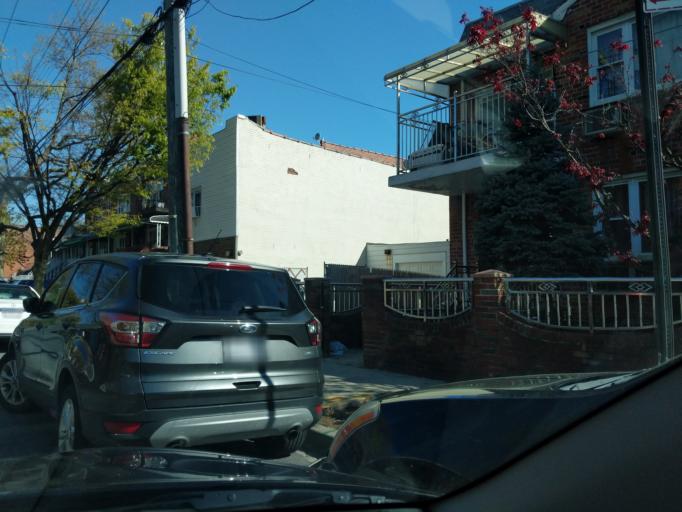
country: US
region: New York
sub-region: Kings County
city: Brooklyn
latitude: 40.6369
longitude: -73.9123
